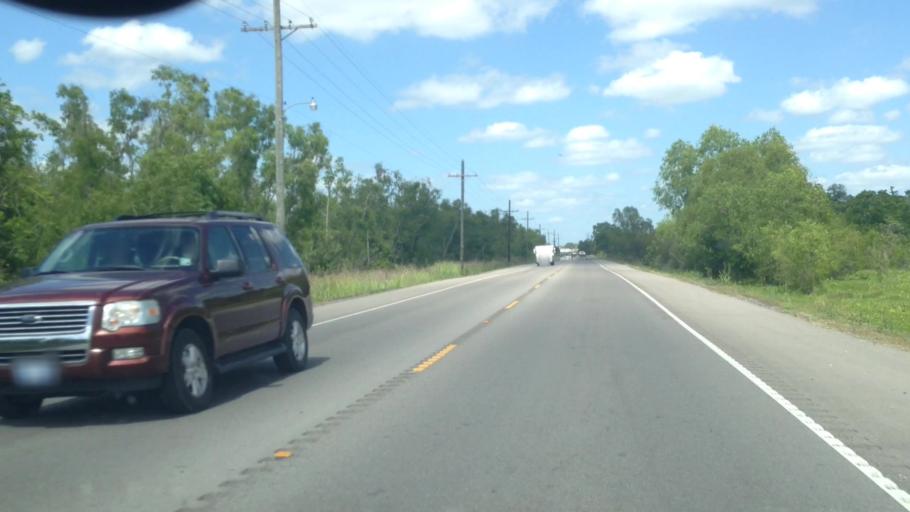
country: US
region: Louisiana
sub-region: Terrebonne Parish
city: Houma
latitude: 29.6369
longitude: -90.6977
